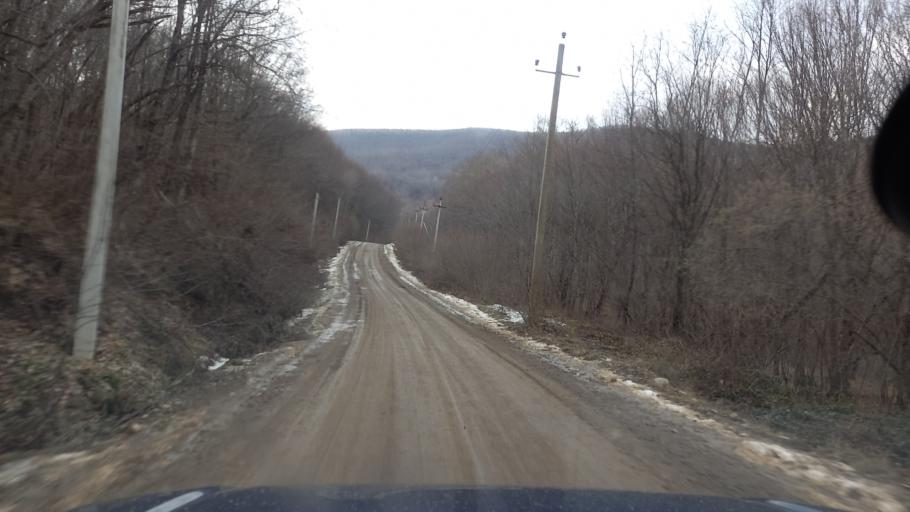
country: RU
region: Adygeya
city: Kamennomostskiy
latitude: 44.1401
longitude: 40.2829
